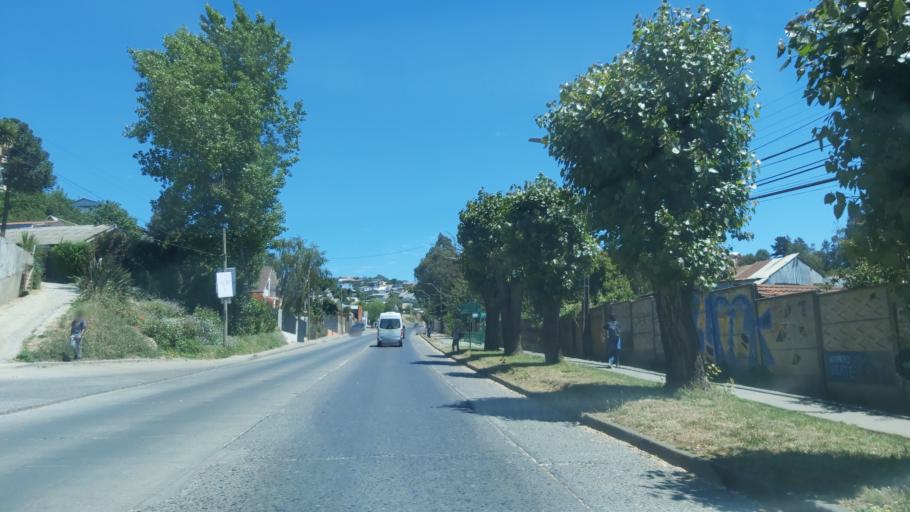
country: CL
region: Maule
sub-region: Provincia de Talca
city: Constitucion
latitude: -35.3348
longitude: -72.4164
